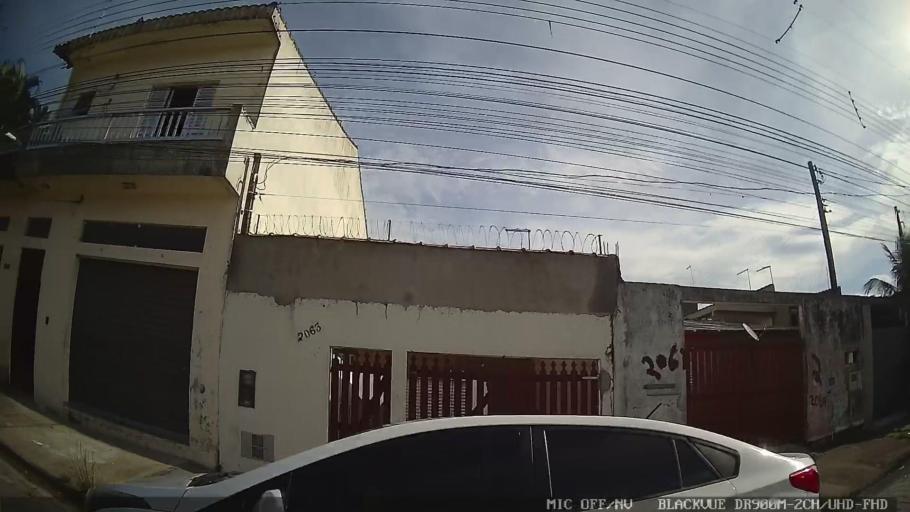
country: BR
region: Sao Paulo
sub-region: Itanhaem
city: Itanhaem
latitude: -24.1544
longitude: -46.7777
